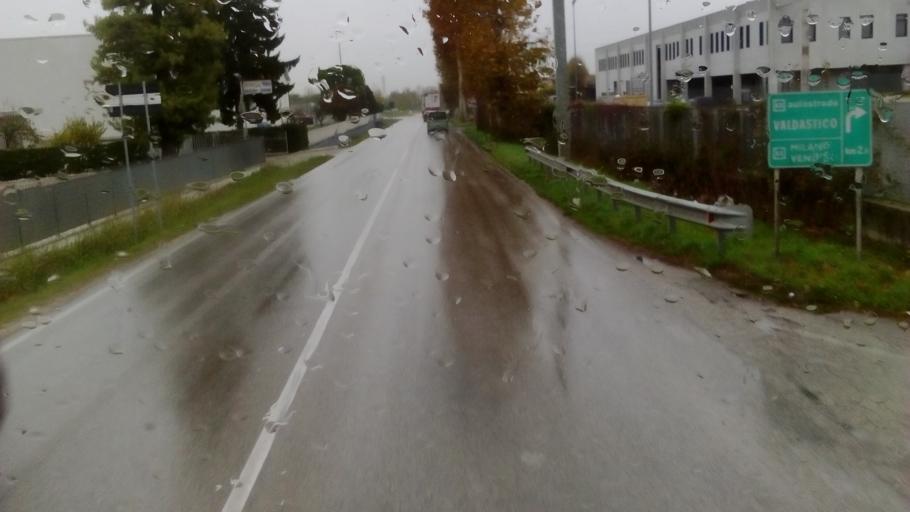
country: IT
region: Veneto
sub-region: Provincia di Vicenza
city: Sandrigo
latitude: 45.6551
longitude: 11.5827
